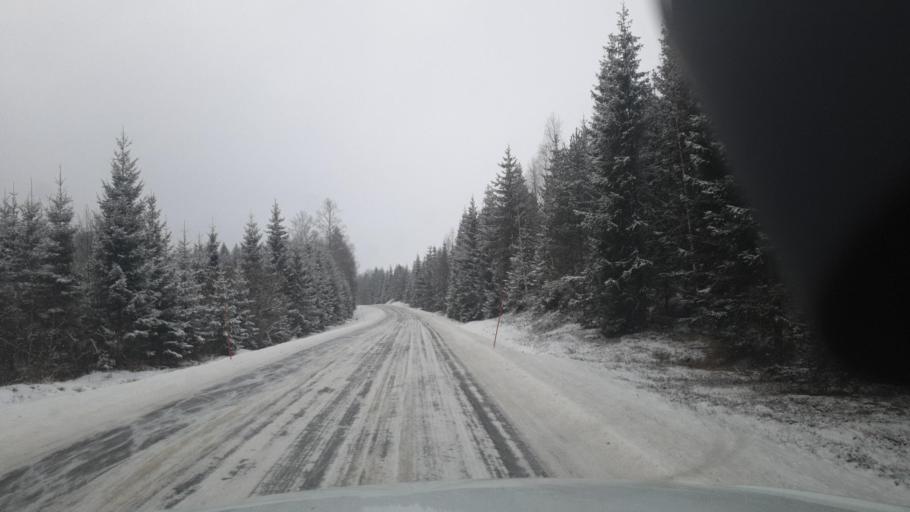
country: SE
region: Vaermland
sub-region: Arvika Kommun
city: Arvika
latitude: 59.9310
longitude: 12.6642
